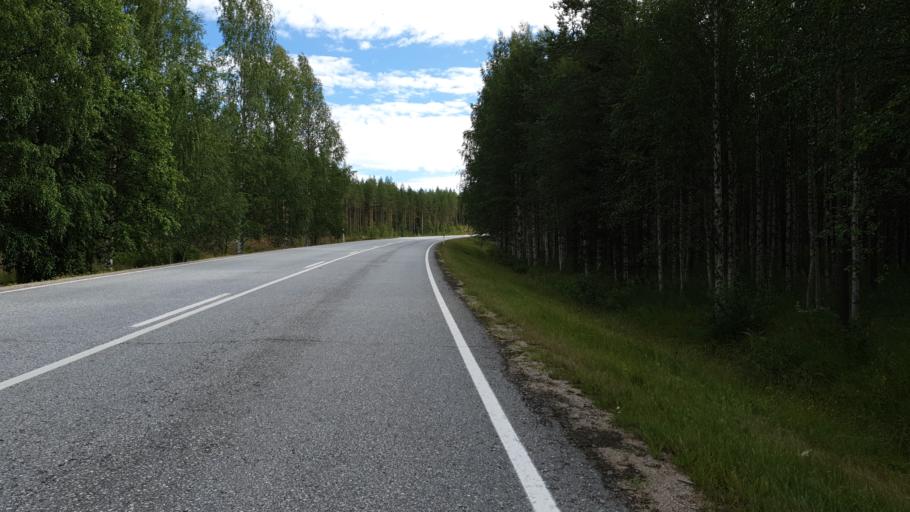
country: FI
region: Kainuu
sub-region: Kehys-Kainuu
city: Kuhmo
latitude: 64.4894
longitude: 29.8136
